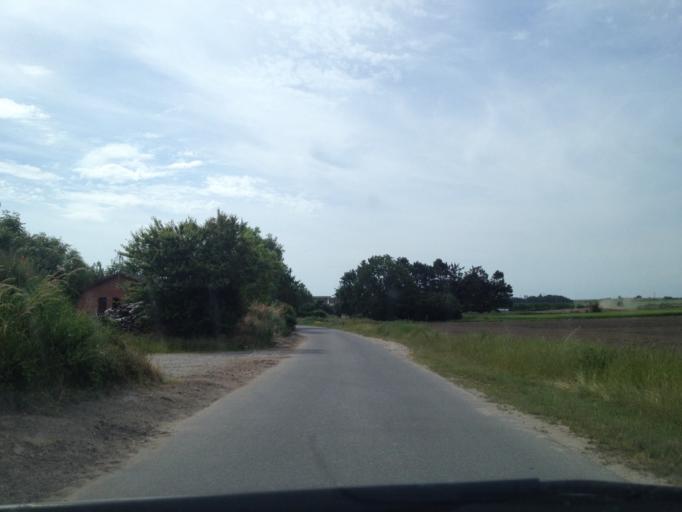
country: DK
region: Central Jutland
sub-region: Samso Kommune
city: Tranebjerg
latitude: 55.9652
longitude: 10.5497
